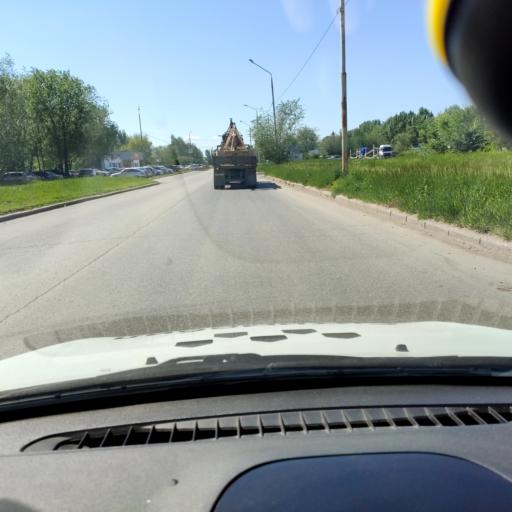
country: RU
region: Samara
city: Podstepki
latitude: 53.5843
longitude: 49.2284
